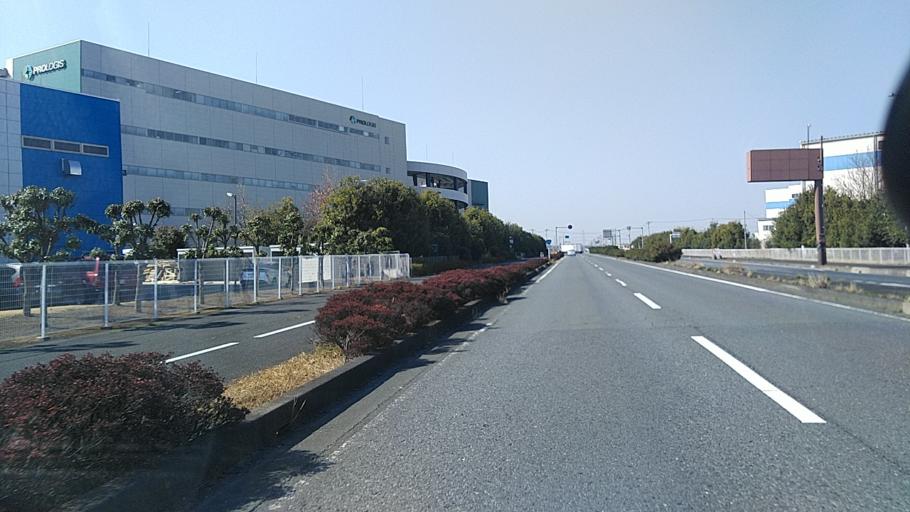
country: JP
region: Saitama
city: Sakado
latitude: 35.9858
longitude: 139.4615
